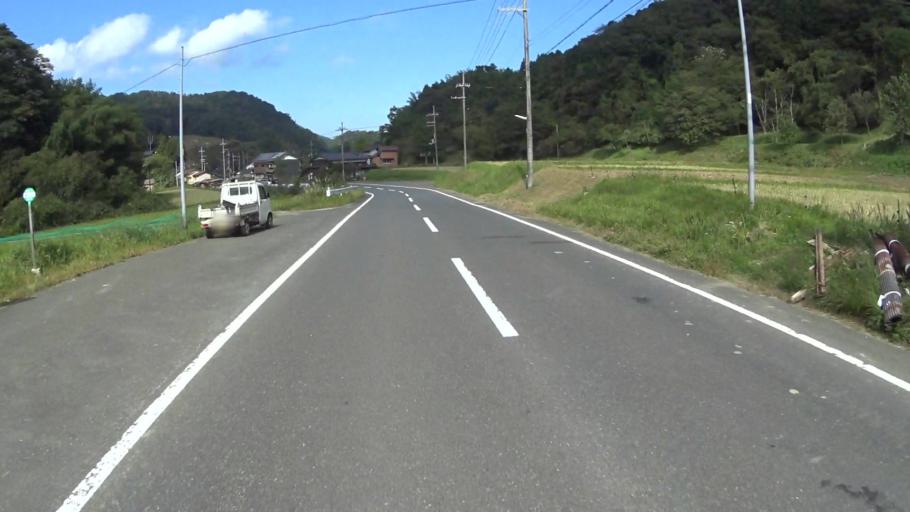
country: JP
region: Kyoto
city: Miyazu
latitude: 35.6954
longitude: 135.2507
